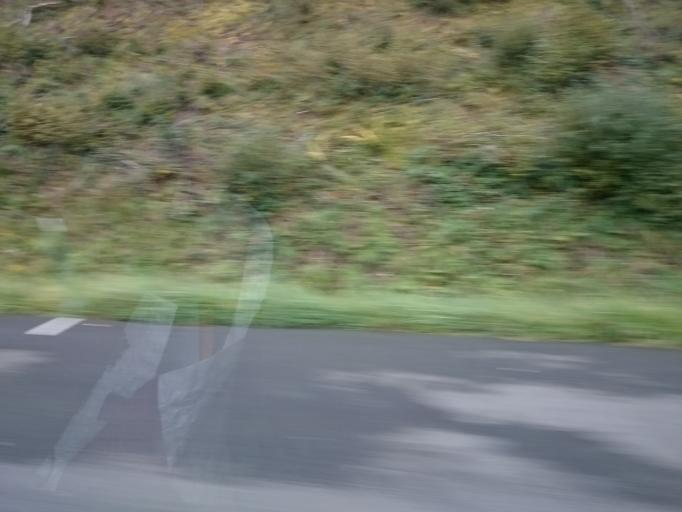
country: FR
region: Brittany
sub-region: Departement du Finistere
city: Plouigneau
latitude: 48.5771
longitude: -3.6412
